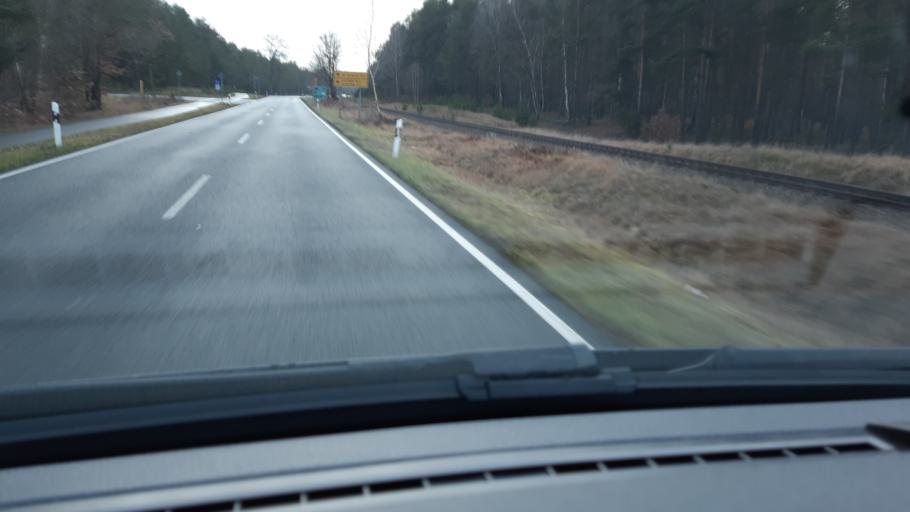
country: DE
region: Brandenburg
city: Zehdenick
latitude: 53.0192
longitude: 13.3726
